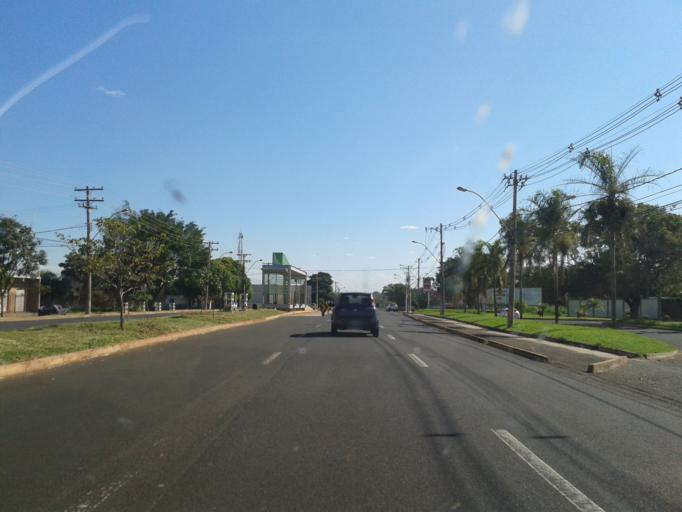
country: BR
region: Minas Gerais
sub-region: Uberaba
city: Uberaba
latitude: -19.7494
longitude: -47.9738
